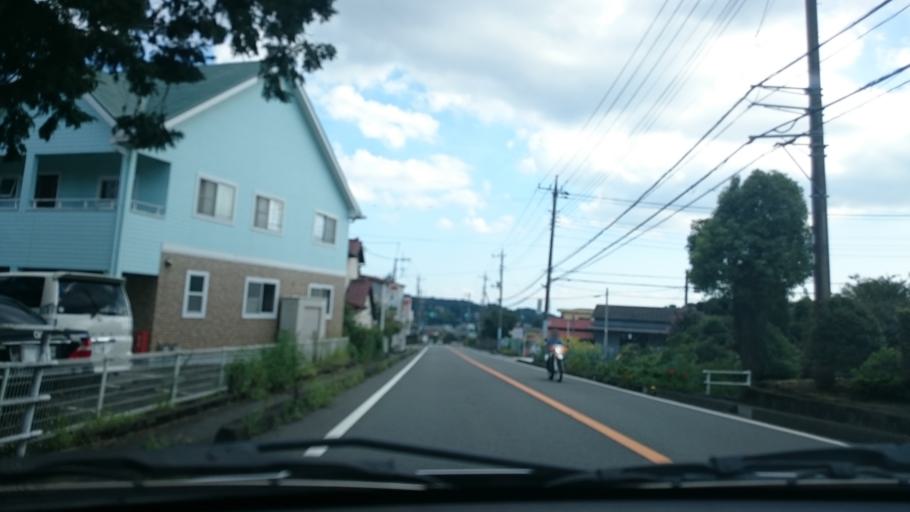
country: JP
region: Shizuoka
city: Gotemba
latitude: 35.2333
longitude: 138.9202
